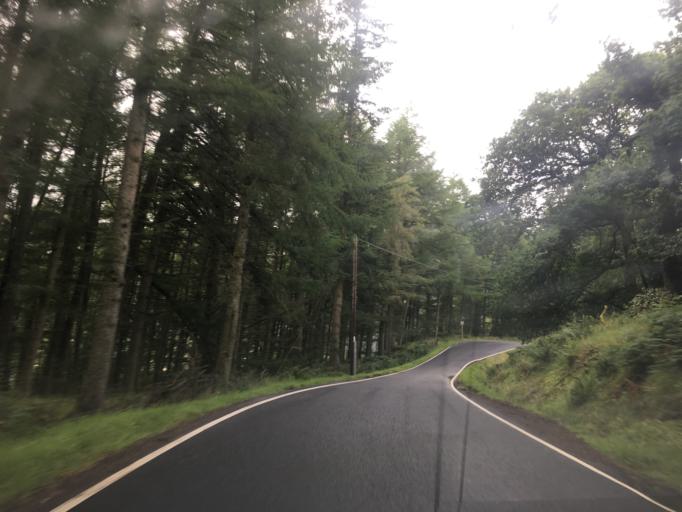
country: GB
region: Scotland
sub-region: Argyll and Bute
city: Port Bannatyne
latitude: 55.9999
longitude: -5.1152
